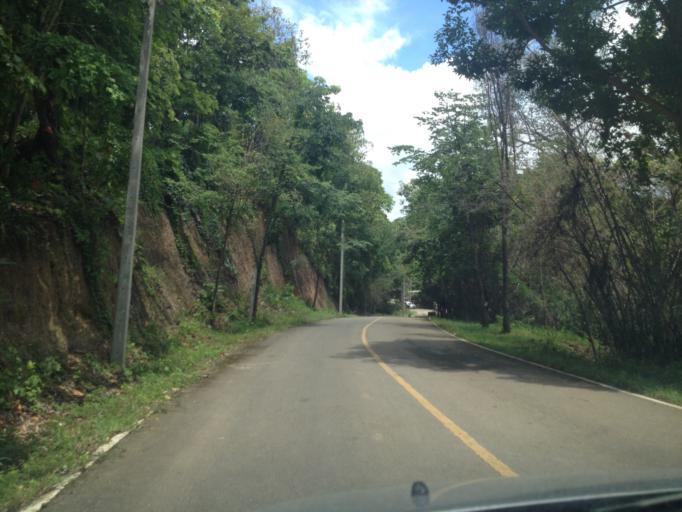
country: TH
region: Chiang Mai
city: Hang Dong
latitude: 18.7121
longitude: 98.8977
